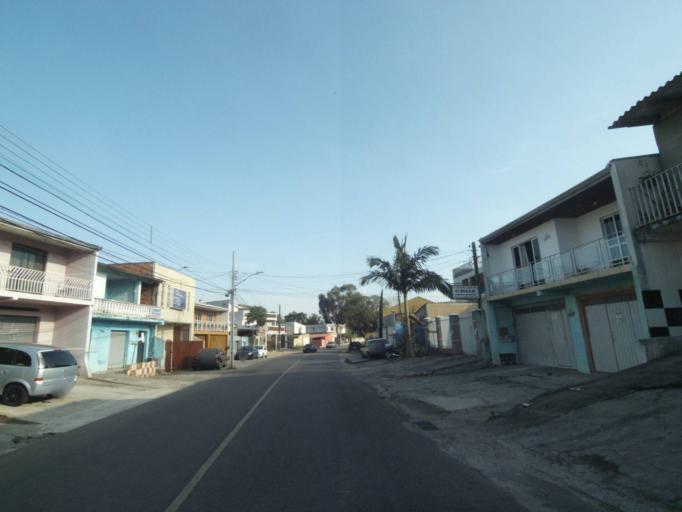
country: BR
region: Parana
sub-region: Curitiba
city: Curitiba
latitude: -25.4890
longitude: -49.3355
